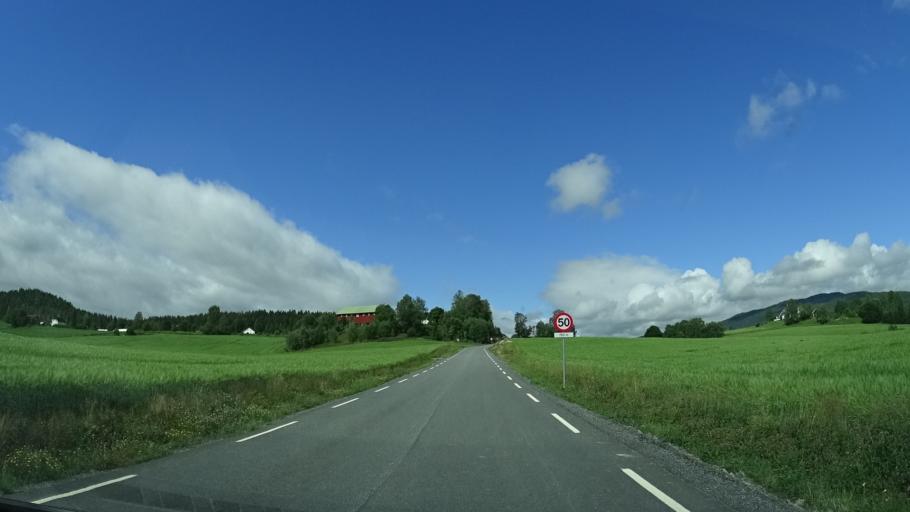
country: NO
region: Buskerud
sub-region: Modum
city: Vikersund
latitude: 60.2305
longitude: 9.9265
